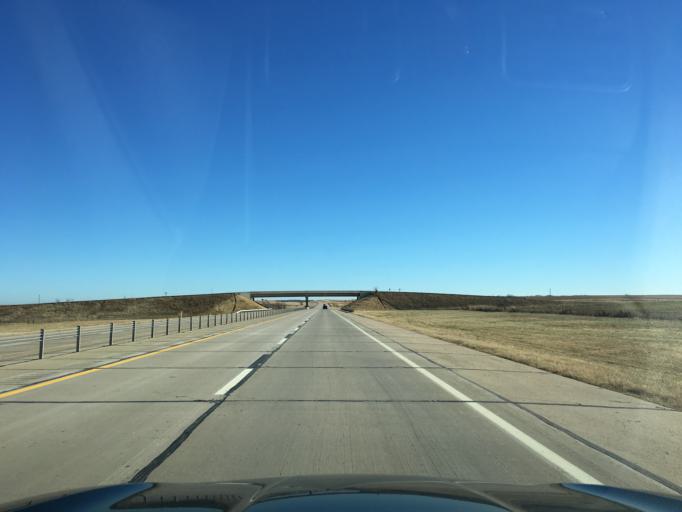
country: US
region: Oklahoma
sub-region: Noble County
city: Perry
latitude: 36.3974
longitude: -97.2321
